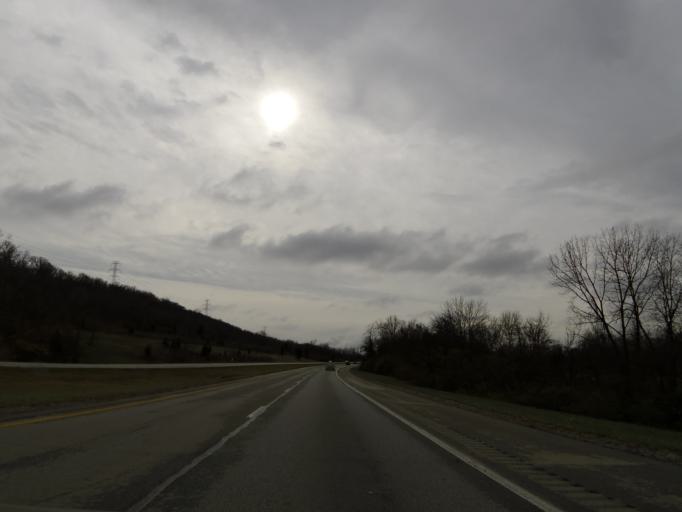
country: US
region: Ohio
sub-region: Hamilton County
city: Cleves
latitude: 39.1945
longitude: -84.7705
